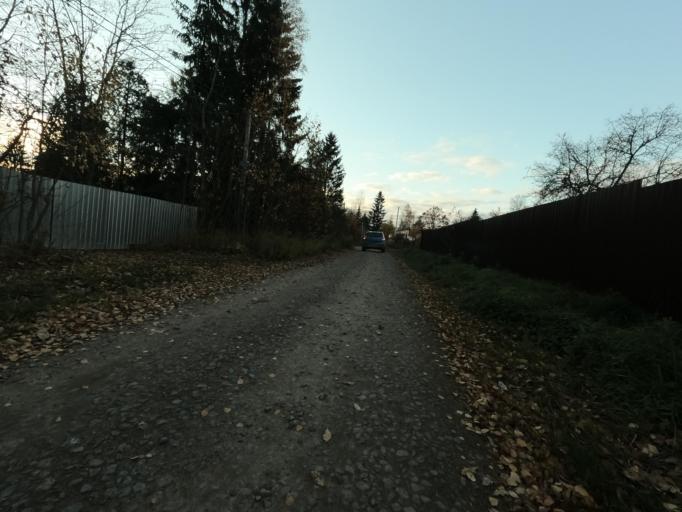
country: RU
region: Leningrad
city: Mga
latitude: 59.7818
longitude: 31.1995
